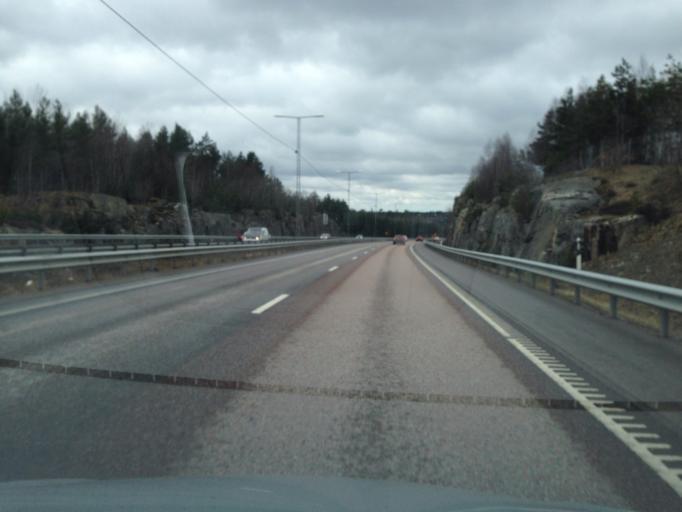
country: SE
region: Stockholm
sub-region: Vallentuna Kommun
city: Vallentuna
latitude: 59.4948
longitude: 18.1749
